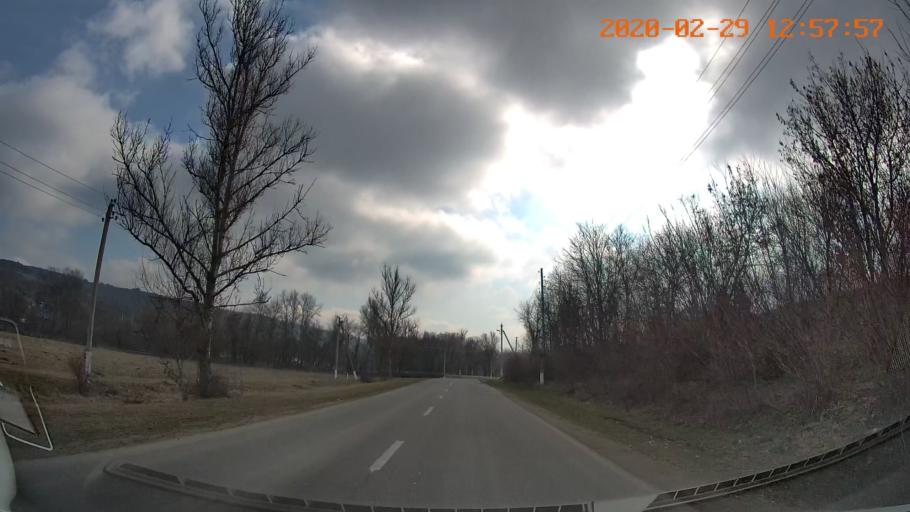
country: MD
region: Telenesti
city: Camenca
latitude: 48.0728
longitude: 28.7175
